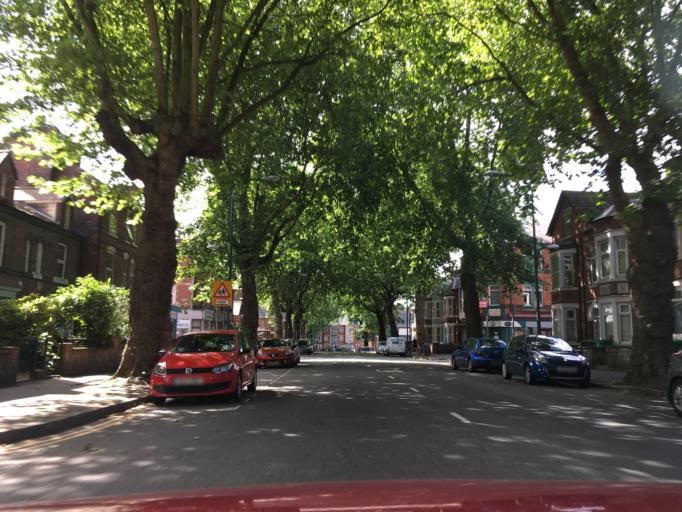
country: GB
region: England
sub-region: Nottingham
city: Nottingham
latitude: 52.9483
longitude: -1.1743
